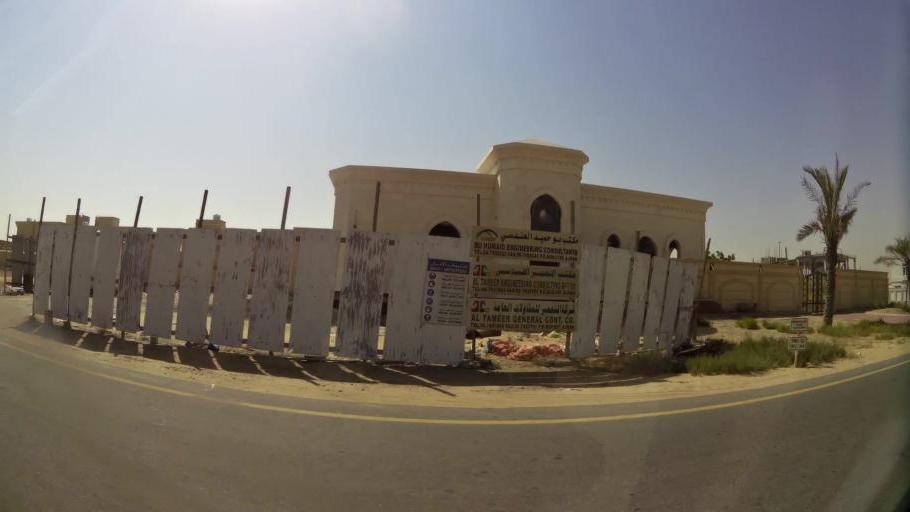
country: AE
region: Ajman
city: Ajman
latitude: 25.4142
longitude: 55.5289
